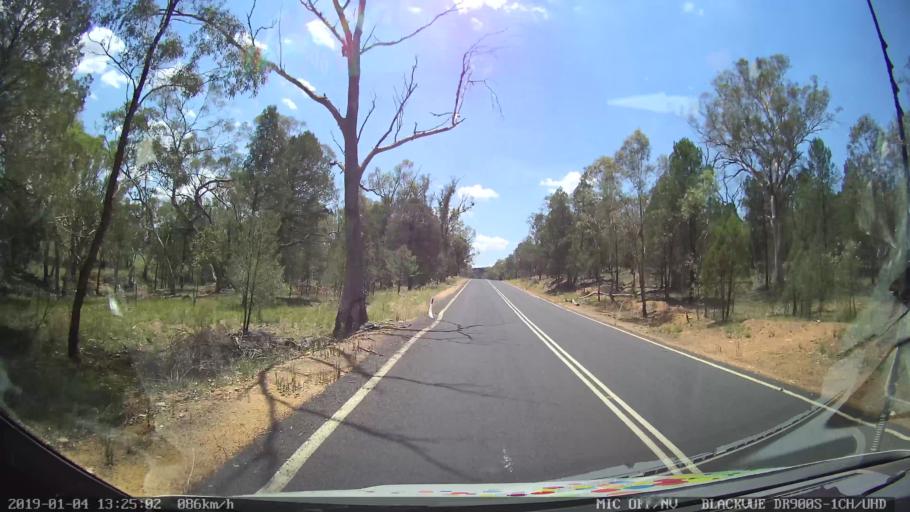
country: AU
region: New South Wales
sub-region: Parkes
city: Peak Hill
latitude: -32.6980
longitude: 148.5543
